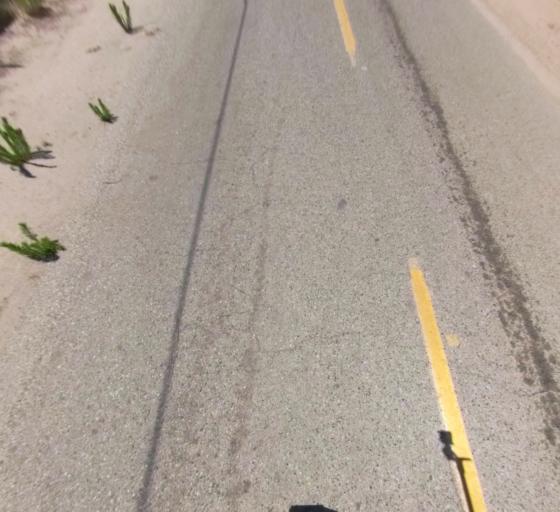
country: US
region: California
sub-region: Madera County
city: Parkwood
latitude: 36.8880
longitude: -120.0105
